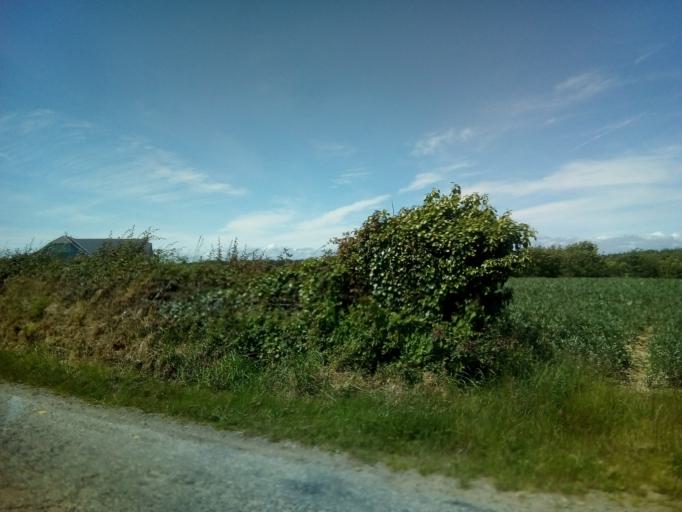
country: IE
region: Munster
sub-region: Waterford
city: Dunmore East
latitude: 52.2344
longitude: -6.8607
